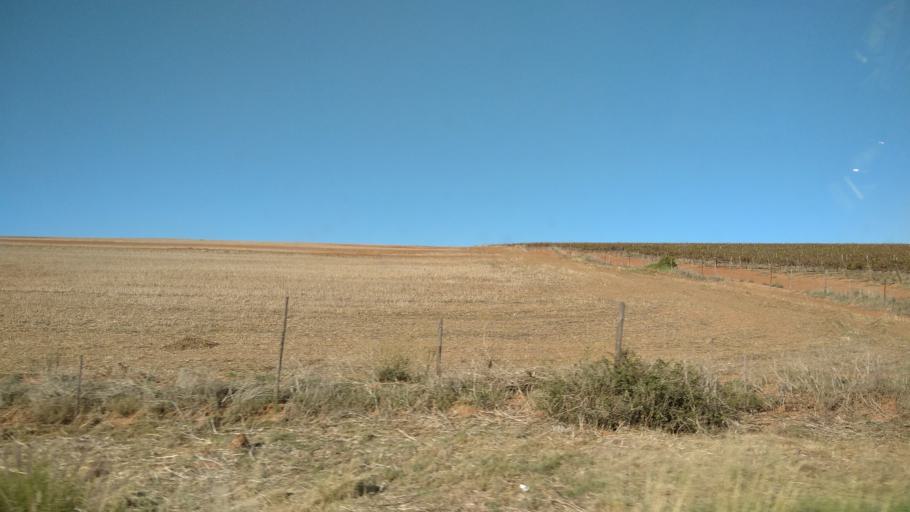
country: ZA
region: Western Cape
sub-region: West Coast District Municipality
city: Malmesbury
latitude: -33.3990
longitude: 18.6883
